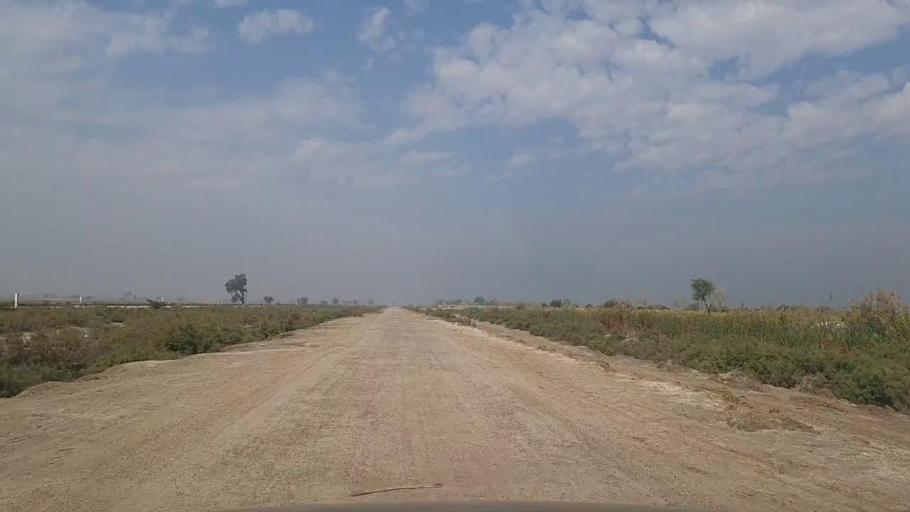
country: PK
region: Sindh
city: Daur
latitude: 26.3892
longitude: 68.3509
